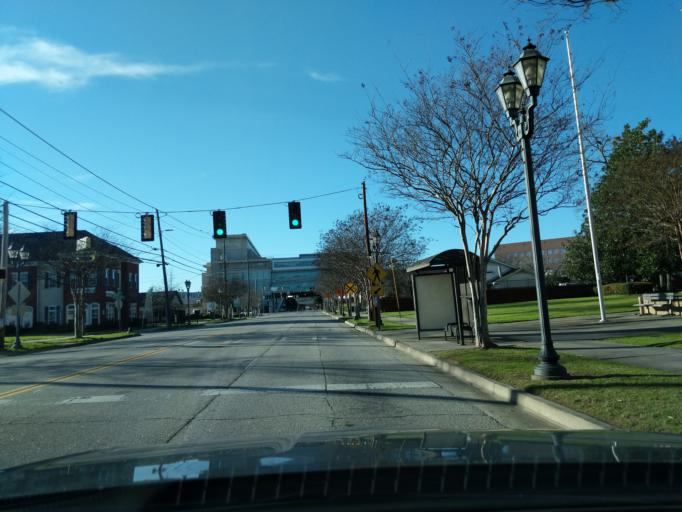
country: US
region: Georgia
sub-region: Richmond County
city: Augusta
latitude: 33.4673
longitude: -81.9837
